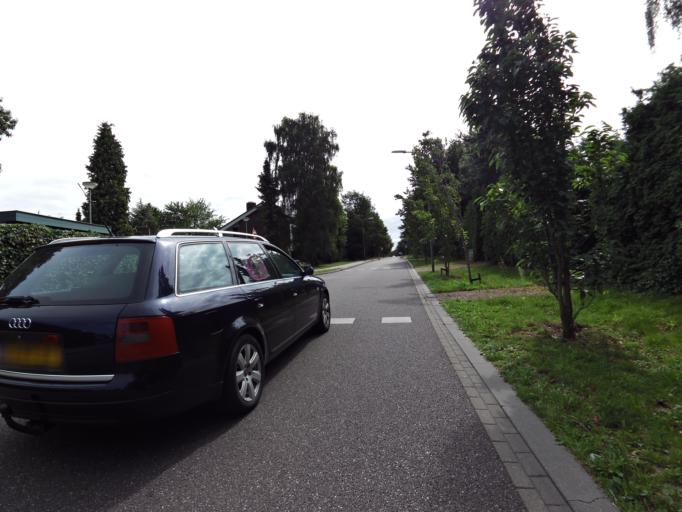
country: NL
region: Limburg
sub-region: Gemeente Onderbanken
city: Merkelbeek
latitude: 50.9542
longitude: 5.9427
